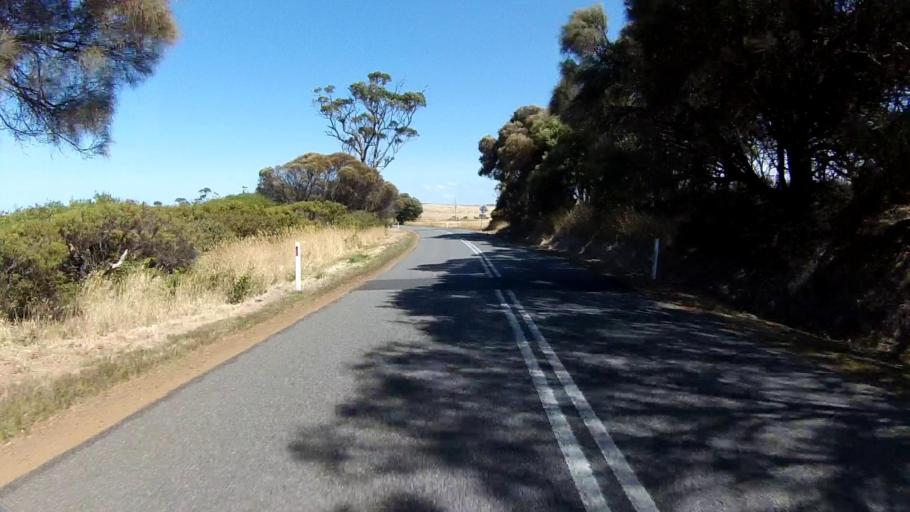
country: AU
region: Tasmania
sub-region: Sorell
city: Sorell
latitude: -42.2425
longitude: 148.0120
